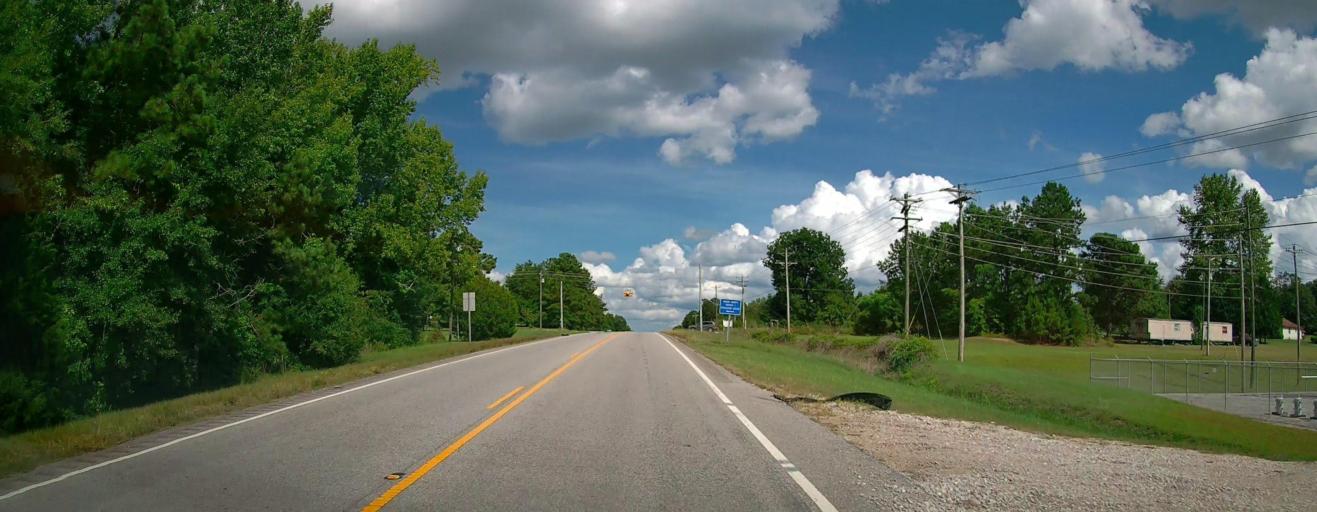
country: US
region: Alabama
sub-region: Macon County
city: Tuskegee
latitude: 32.4637
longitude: -85.5637
